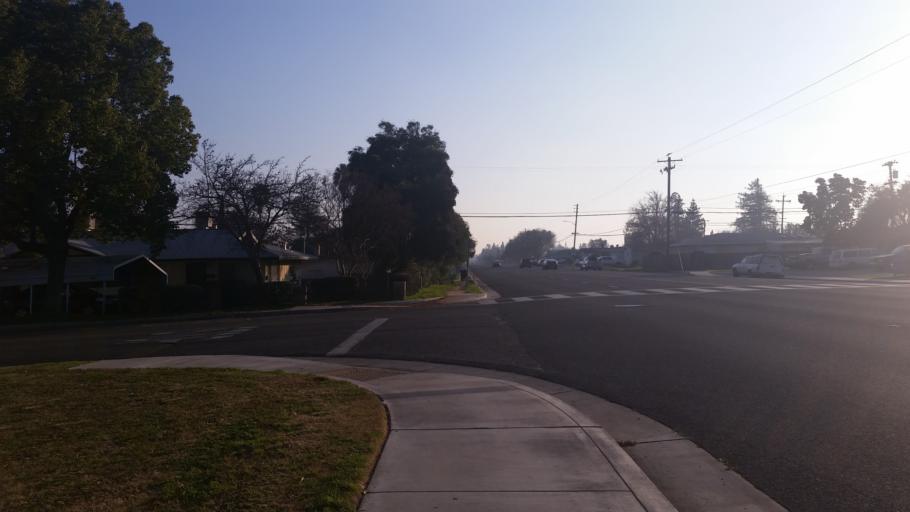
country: US
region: California
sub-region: Merced County
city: Atwater
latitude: 37.3579
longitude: -120.5958
